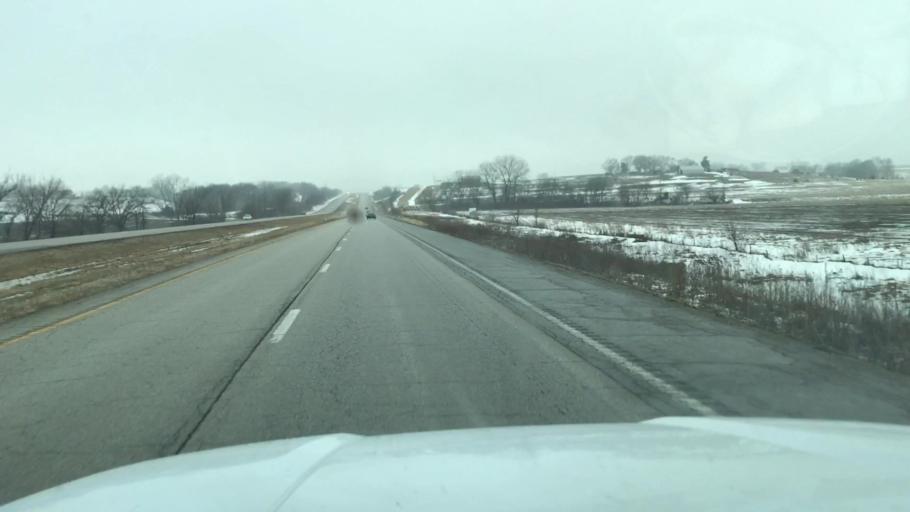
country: US
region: Missouri
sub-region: Clinton County
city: Gower
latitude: 39.7476
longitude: -94.6652
